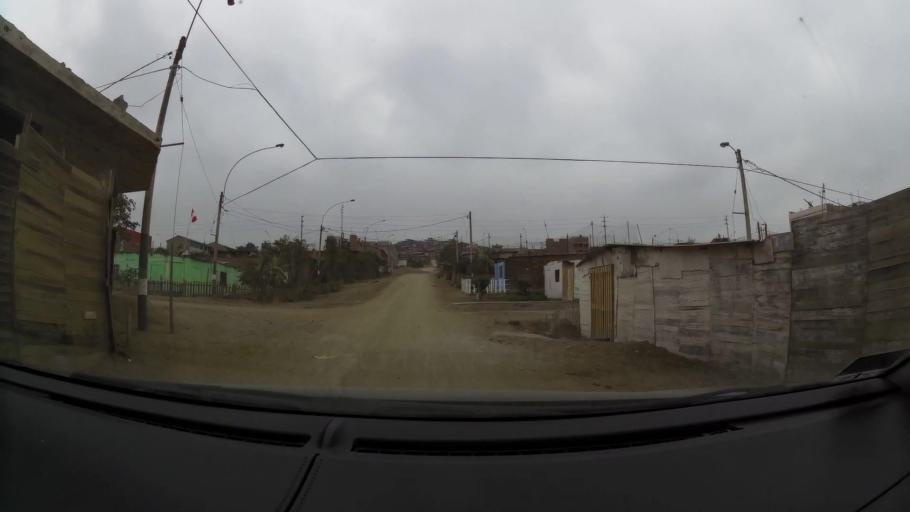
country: PE
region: Lima
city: Ventanilla
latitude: -11.8511
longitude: -77.1466
